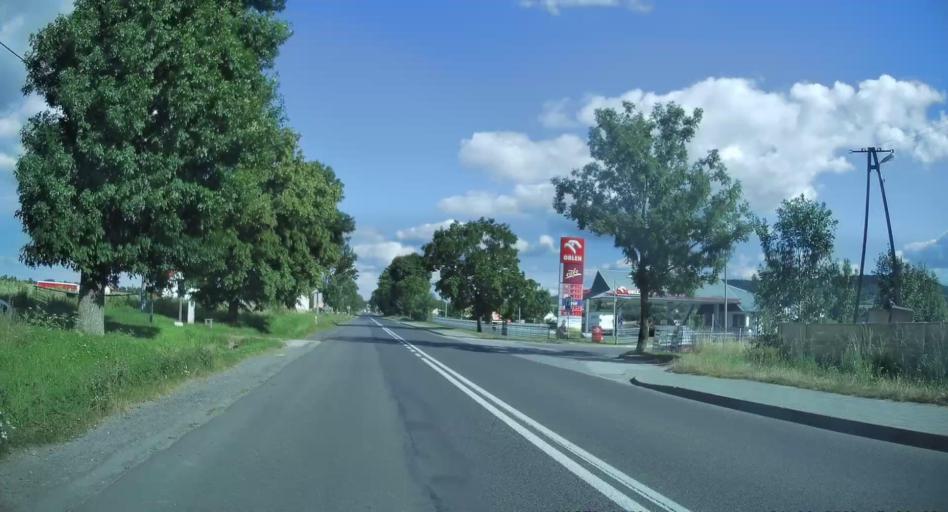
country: PL
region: Swietokrzyskie
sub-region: Powiat kielecki
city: Bodzentyn
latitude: 50.9492
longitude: 20.9306
